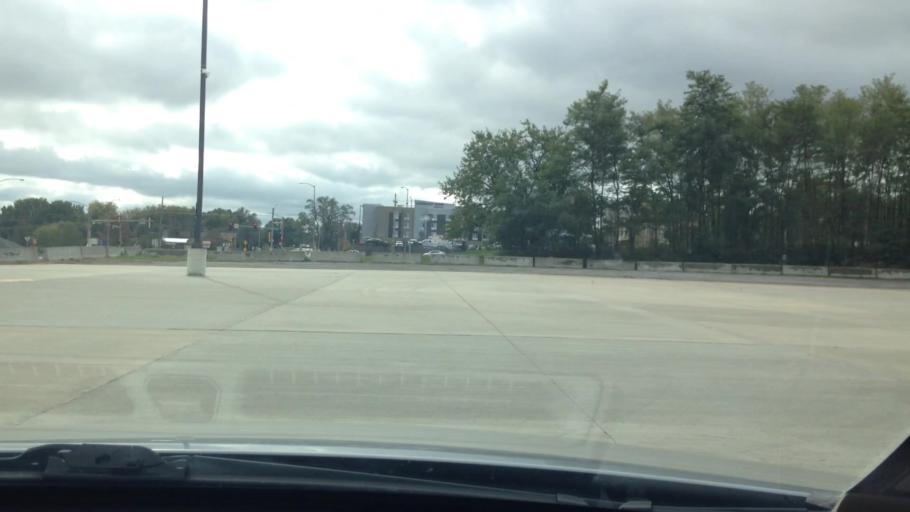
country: US
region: Kansas
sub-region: Leavenworth County
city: Leavenworth
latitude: 39.3303
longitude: -94.9168
